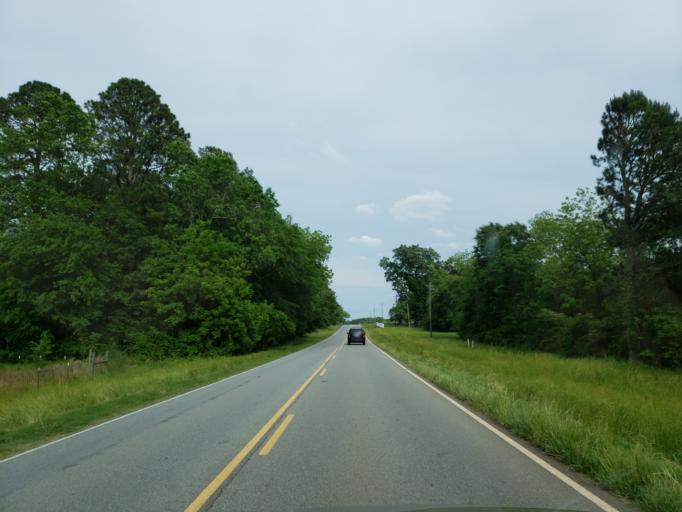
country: US
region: Georgia
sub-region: Dooly County
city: Vienna
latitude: 32.1125
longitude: -83.8517
